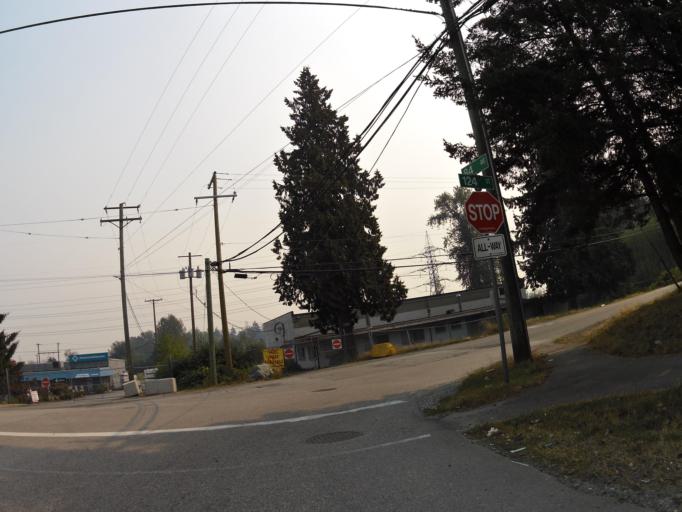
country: CA
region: British Columbia
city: Delta
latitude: 49.1557
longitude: -122.8794
